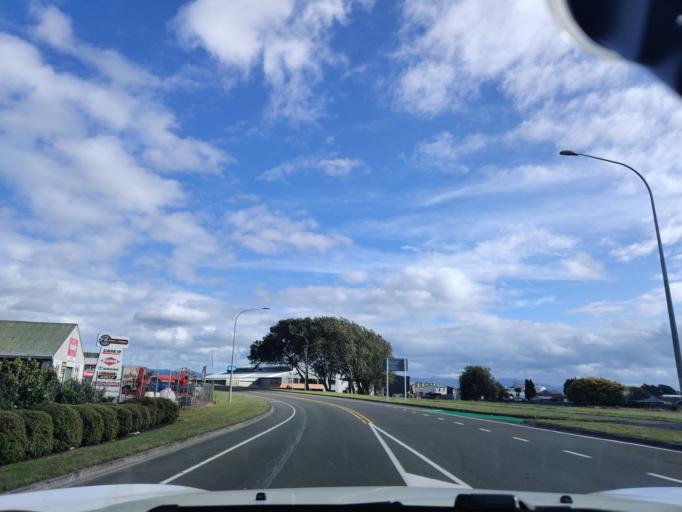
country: NZ
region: Manawatu-Wanganui
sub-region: Palmerston North City
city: Palmerston North
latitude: -40.3254
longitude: 175.6254
